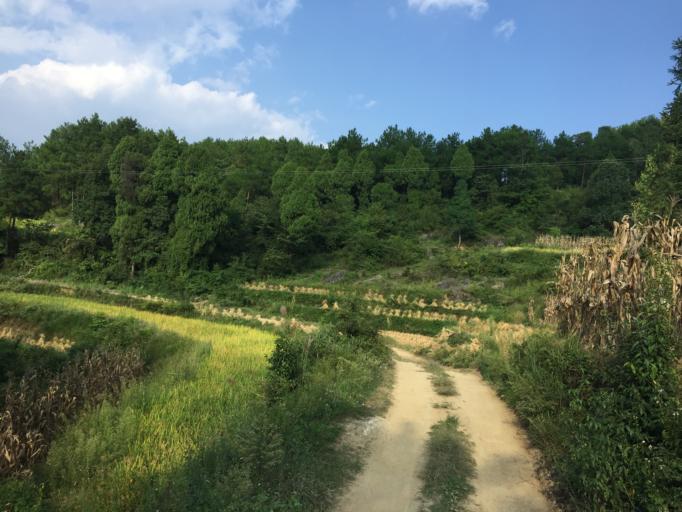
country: CN
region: Guizhou Sheng
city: Shiqian
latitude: 27.6017
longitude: 108.0117
